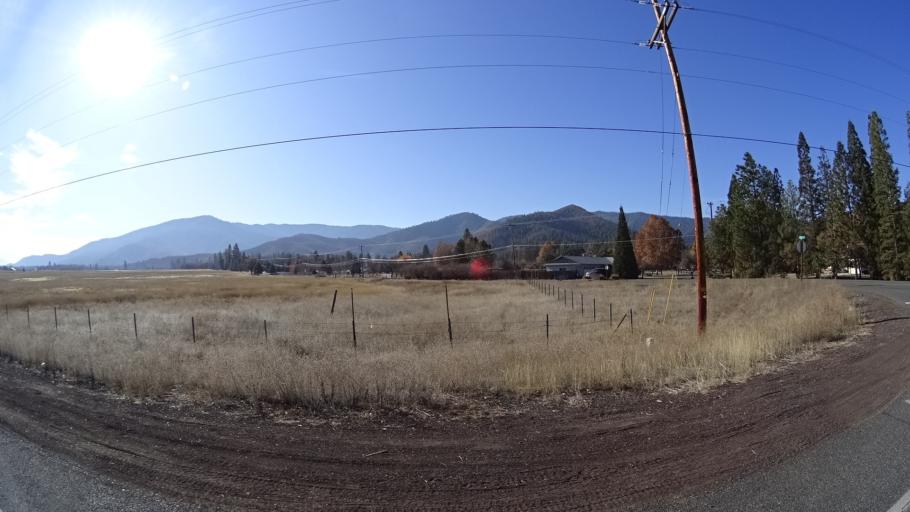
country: US
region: California
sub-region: Siskiyou County
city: Yreka
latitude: 41.6822
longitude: -122.6345
